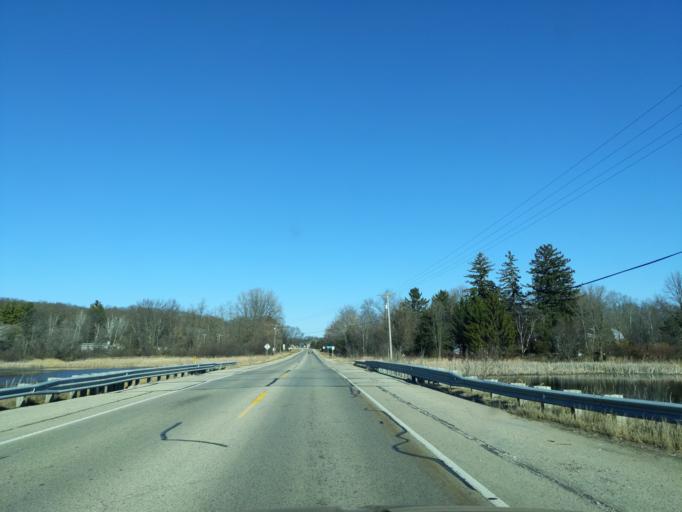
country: US
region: Wisconsin
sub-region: Waushara County
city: Wautoma
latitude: 44.0776
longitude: -89.2927
